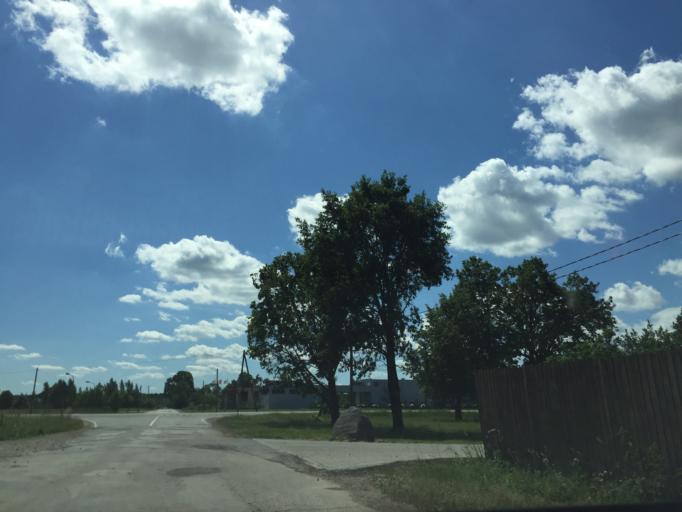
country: LV
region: Marupe
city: Marupe
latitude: 56.8843
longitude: 23.9765
